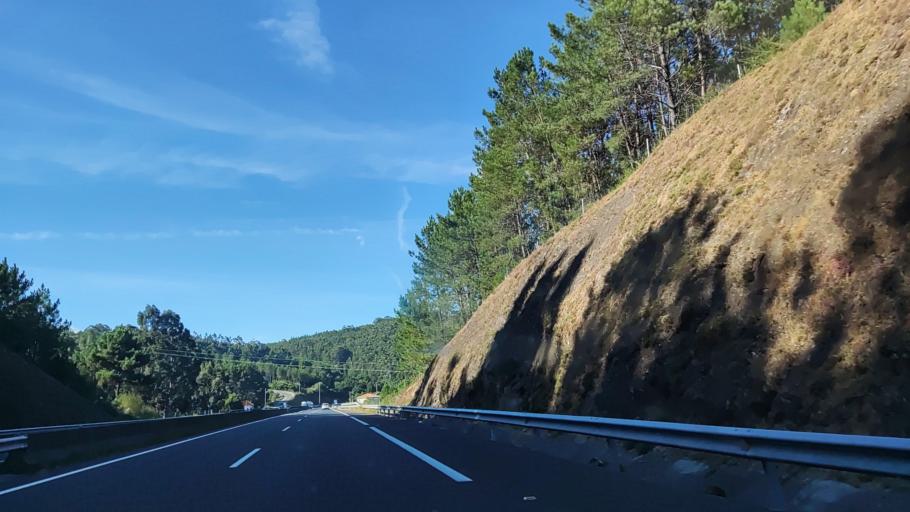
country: ES
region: Galicia
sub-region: Provincia da Coruna
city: Boiro
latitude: 42.6383
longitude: -8.9112
